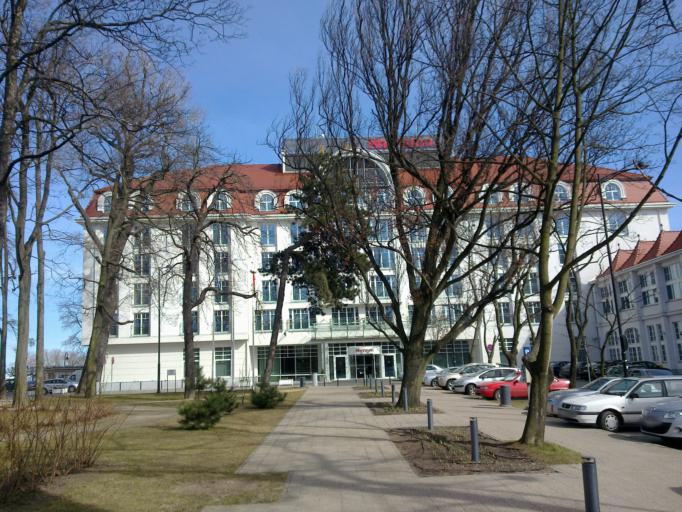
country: PL
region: Pomeranian Voivodeship
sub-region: Sopot
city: Sopot
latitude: 54.4464
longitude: 18.5680
